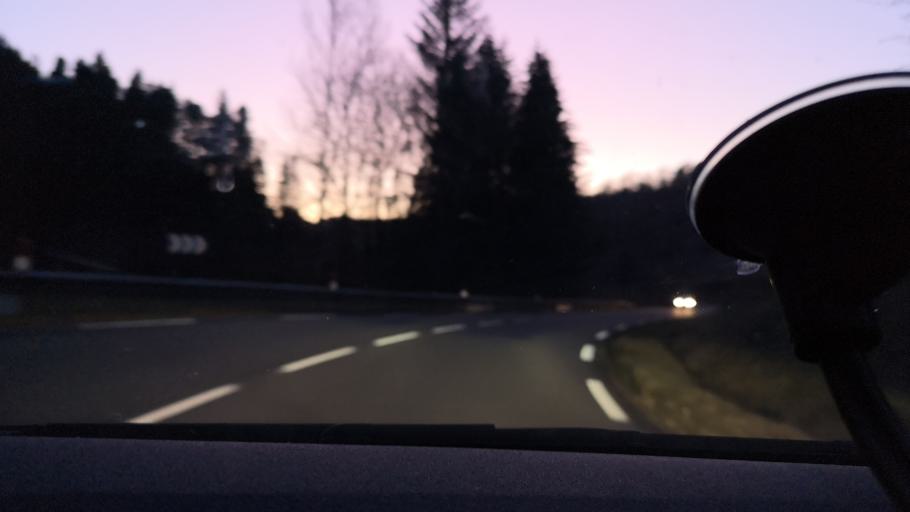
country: FR
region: Franche-Comte
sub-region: Departement du Jura
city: Champagnole
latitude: 46.7730
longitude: 5.9897
